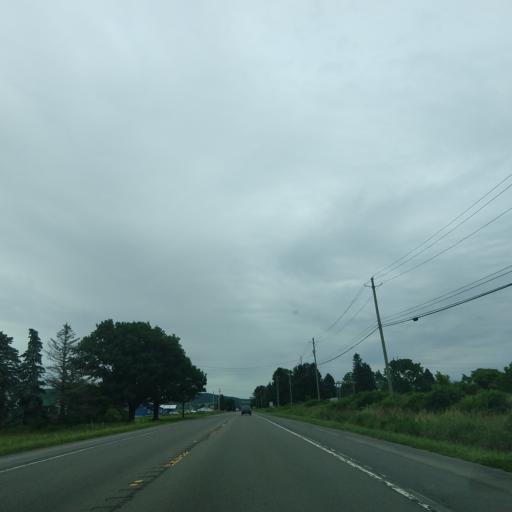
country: US
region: New York
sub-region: Tompkins County
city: Dryden
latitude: 42.4897
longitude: -76.3252
